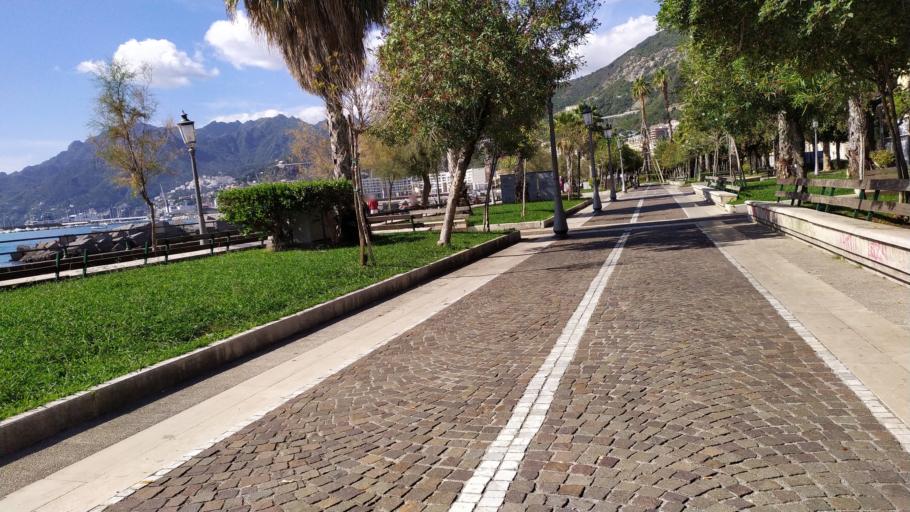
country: IT
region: Campania
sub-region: Provincia di Salerno
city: Capezzano Inferiore
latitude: 40.6763
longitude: 14.7632
